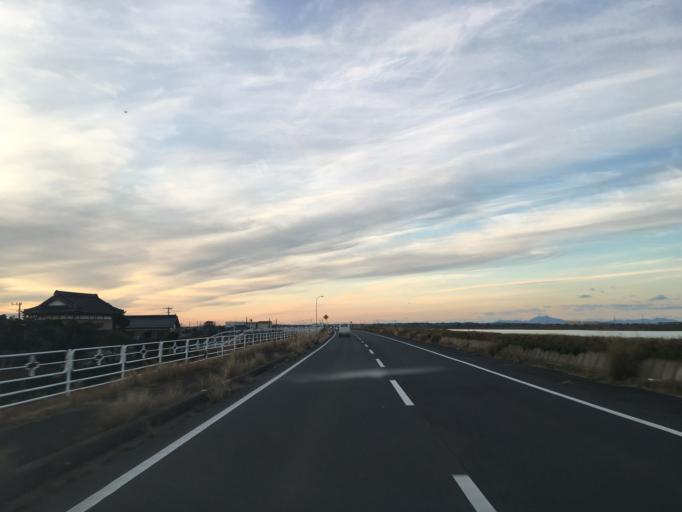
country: JP
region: Chiba
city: Katori-shi
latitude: 35.9127
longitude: 140.4728
